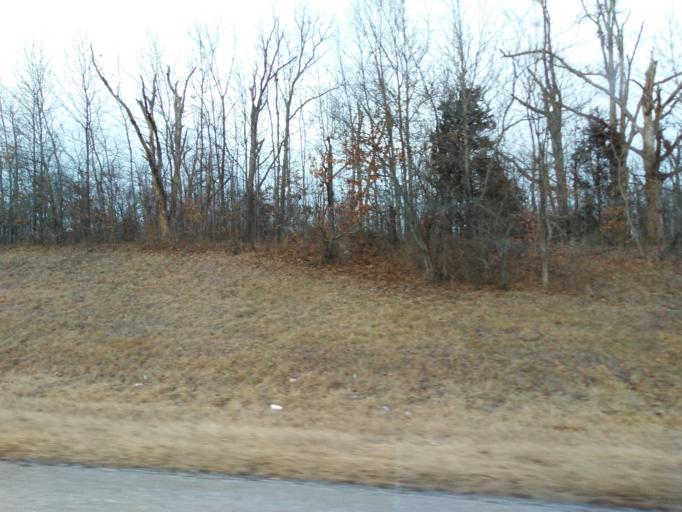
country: US
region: Illinois
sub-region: Clinton County
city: Wamac
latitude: 38.3642
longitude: -89.0842
